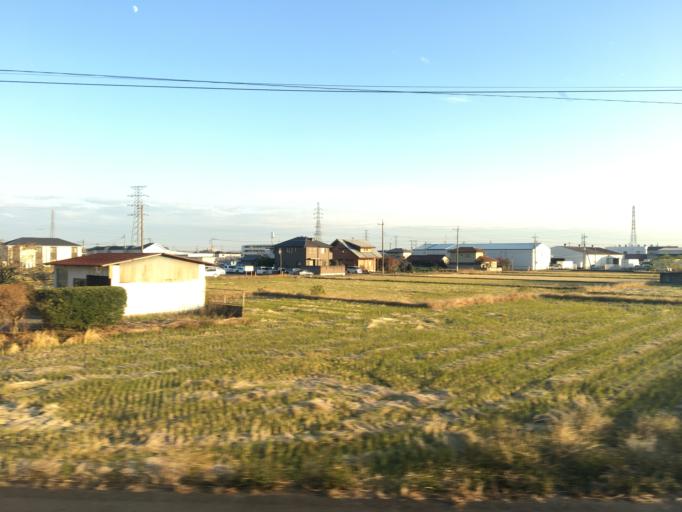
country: JP
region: Gunma
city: Maebashi-shi
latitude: 36.3710
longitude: 139.0363
